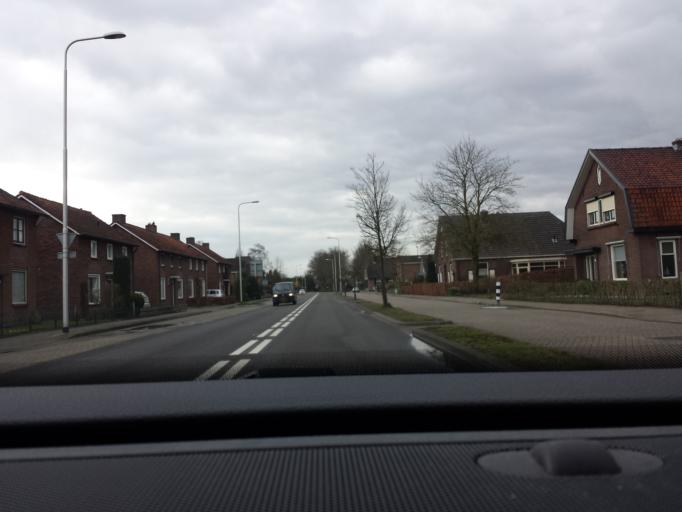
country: NL
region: Gelderland
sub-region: Oude IJsselstreek
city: Varsseveld
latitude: 51.9381
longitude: 6.4628
